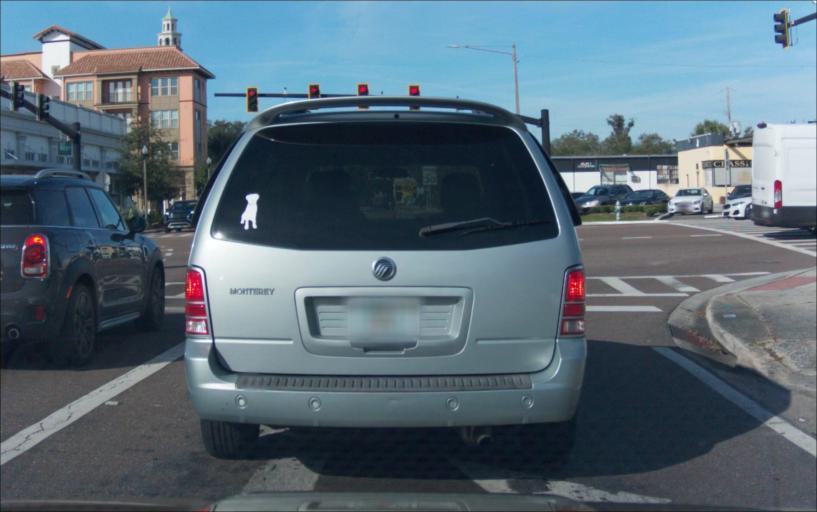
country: US
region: Florida
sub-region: Orange County
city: Maitland
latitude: 28.6325
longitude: -81.3684
